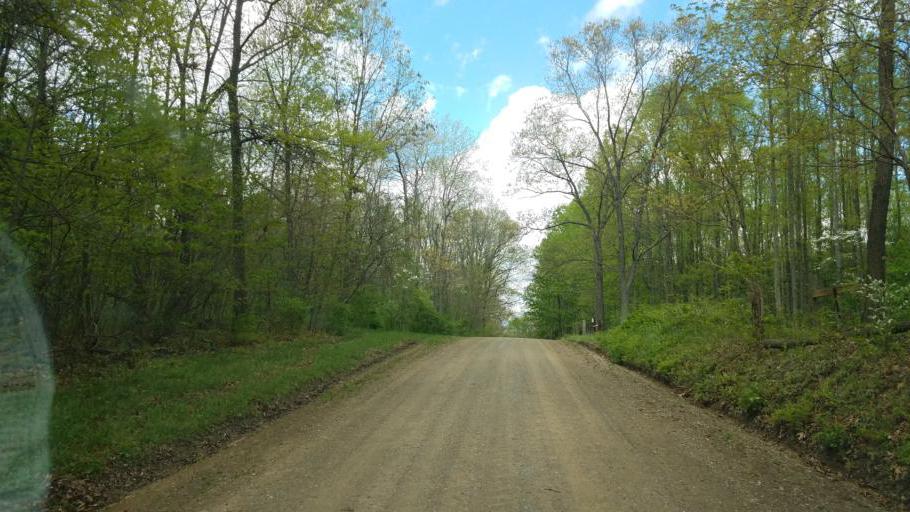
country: US
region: Ohio
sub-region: Knox County
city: Danville
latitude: 40.5384
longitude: -82.2469
